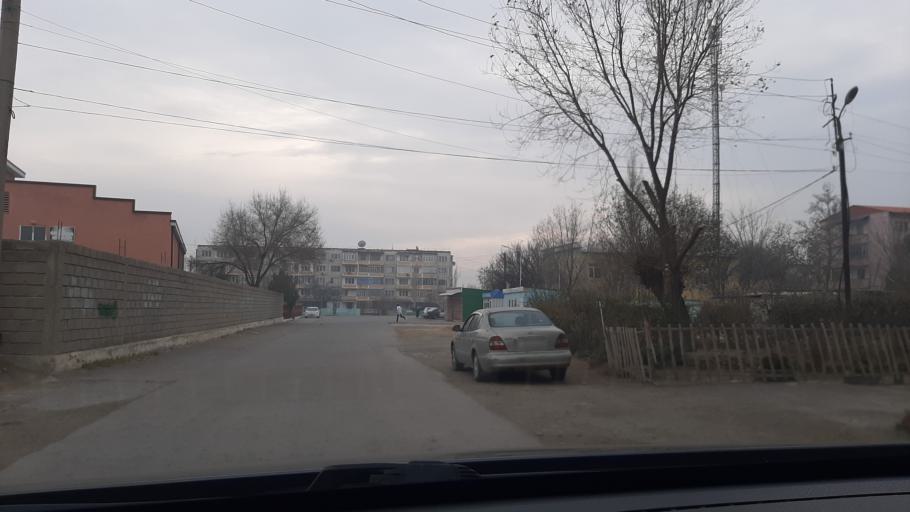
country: TJ
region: Viloyati Sughd
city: Palos
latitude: 40.2618
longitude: 69.7929
